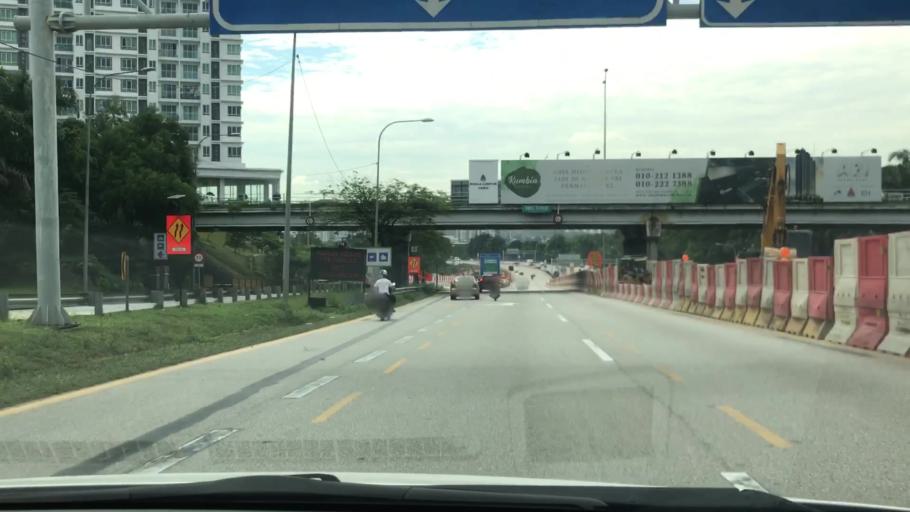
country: MY
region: Kuala Lumpur
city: Kuala Lumpur
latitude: 3.1059
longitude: 101.6935
